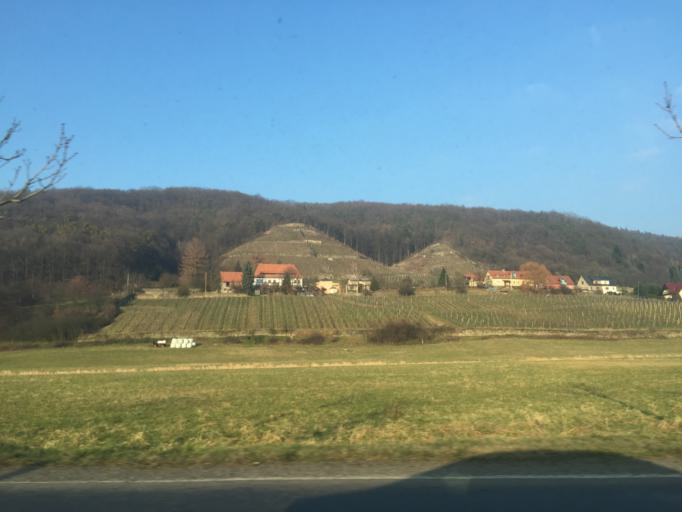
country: DE
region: Saxony
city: Heidenau
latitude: 51.0043
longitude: 13.8878
